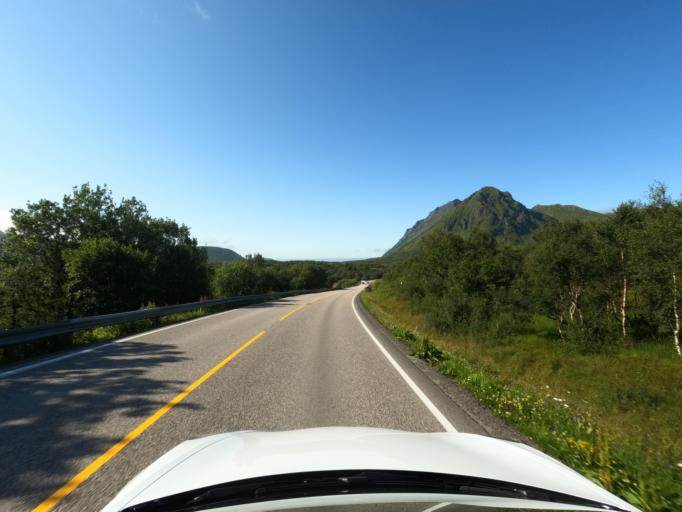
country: NO
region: Nordland
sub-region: Vestvagoy
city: Evjen
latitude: 68.2615
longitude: 13.9849
